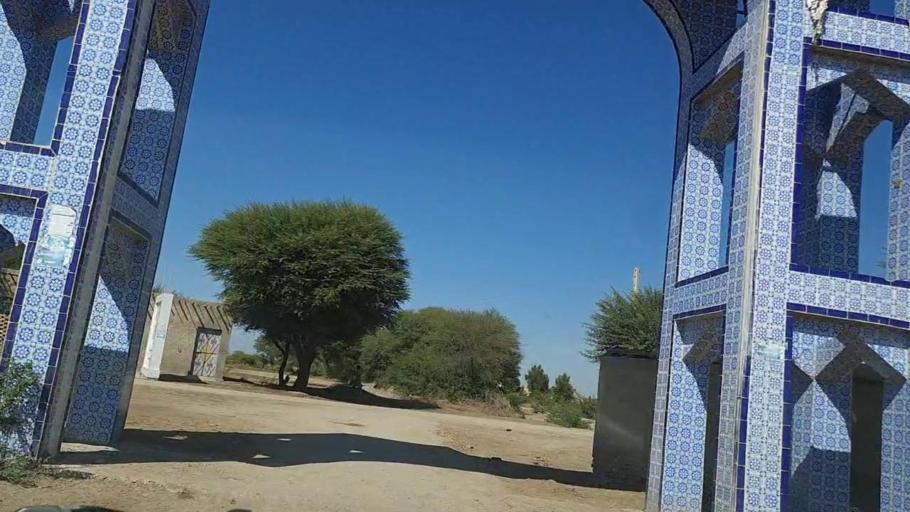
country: PK
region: Sindh
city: Dhoro Naro
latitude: 25.5349
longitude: 69.5008
